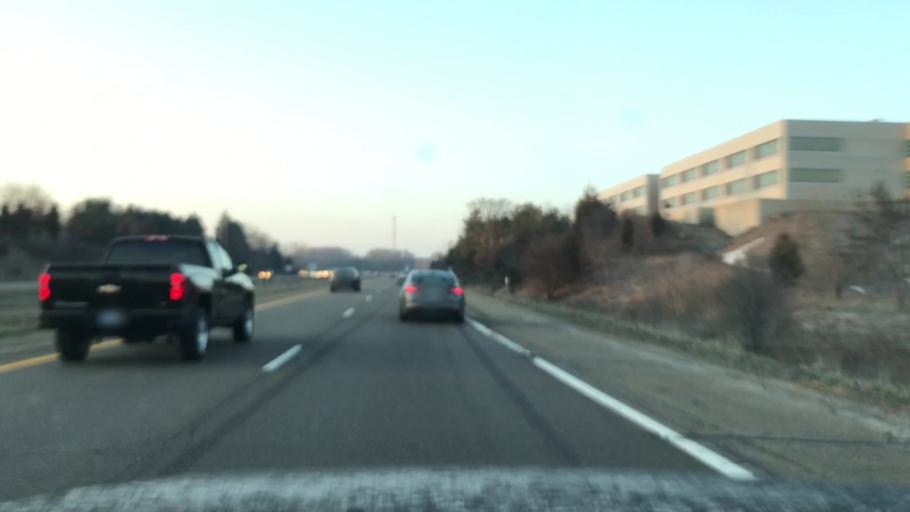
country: US
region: Michigan
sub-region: Kent County
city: East Grand Rapids
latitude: 42.9411
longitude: -85.5667
